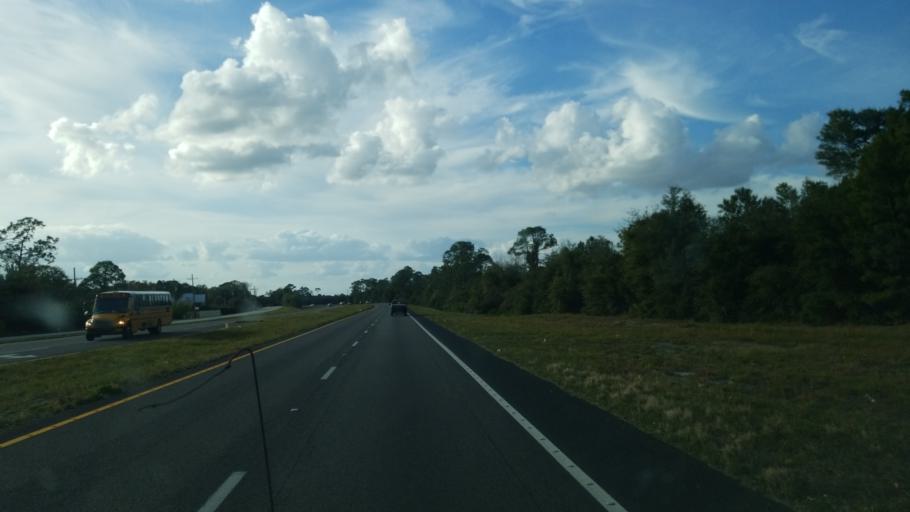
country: US
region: Florida
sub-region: Osceola County
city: Saint Cloud
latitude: 28.2388
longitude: -81.1963
